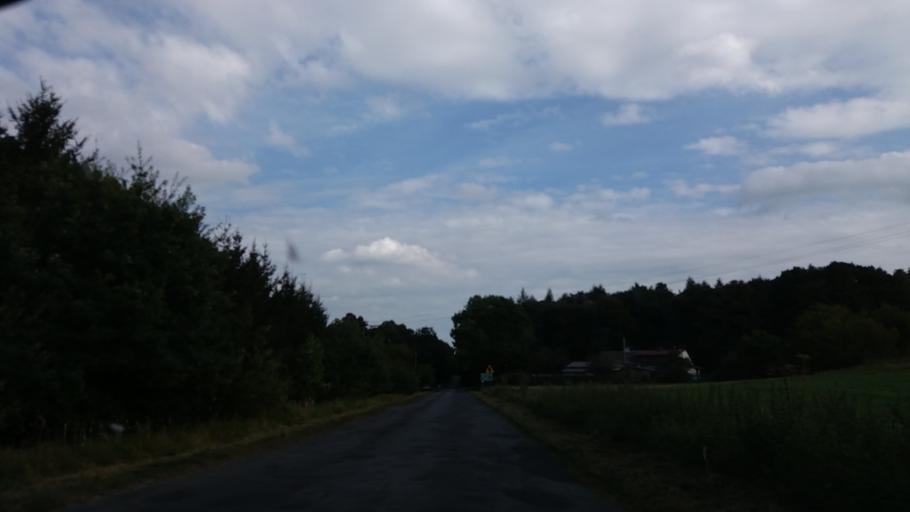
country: PL
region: West Pomeranian Voivodeship
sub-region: Powiat stargardzki
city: Dolice
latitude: 53.2414
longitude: 15.2359
